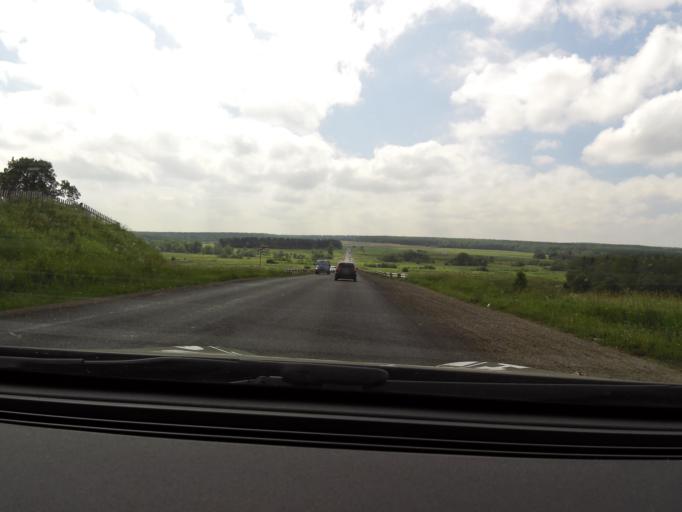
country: RU
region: Perm
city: Bershet'
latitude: 57.7248
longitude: 56.3723
